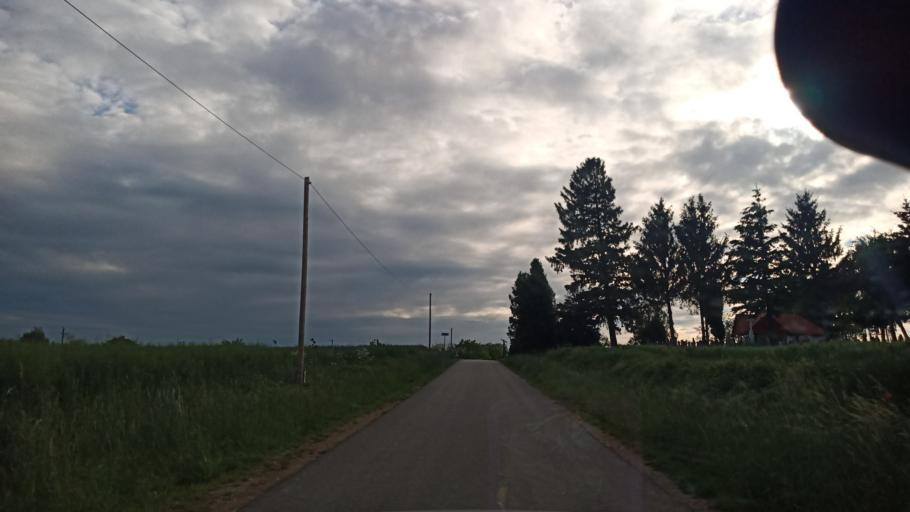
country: HU
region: Zala
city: Pacsa
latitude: 46.7496
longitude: 17.0157
